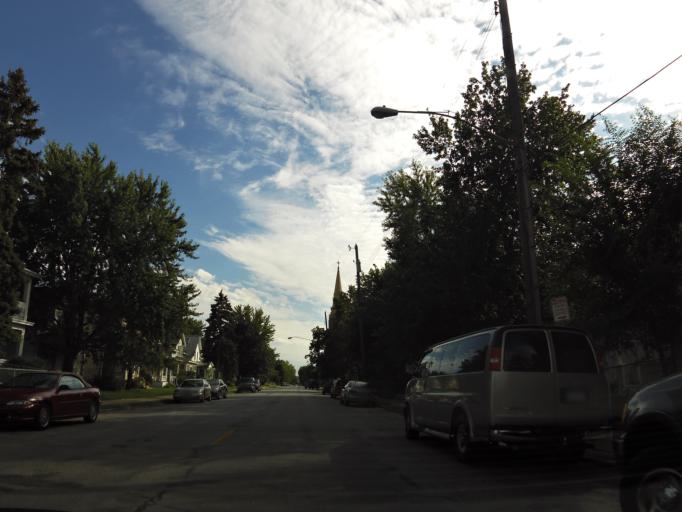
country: US
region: Minnesota
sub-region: Hennepin County
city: Minneapolis
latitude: 45.0027
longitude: -93.2525
